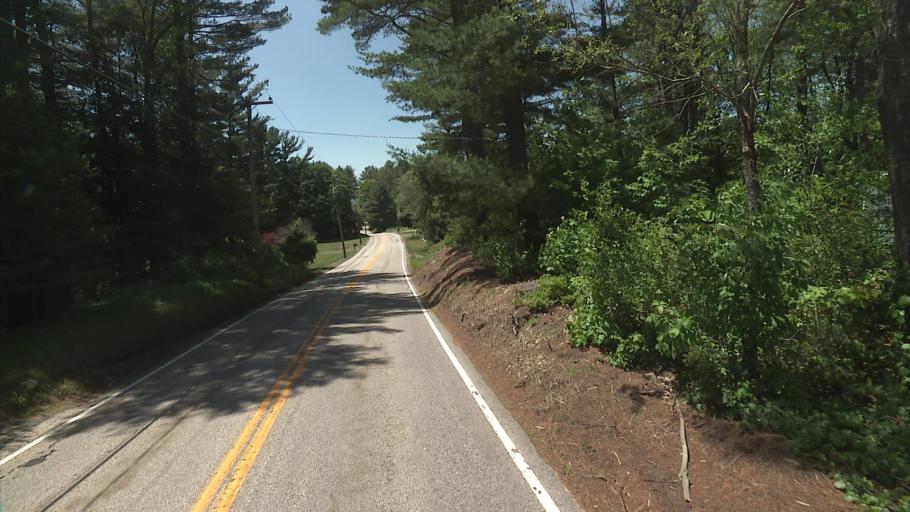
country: US
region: Connecticut
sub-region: Tolland County
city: Stafford Springs
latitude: 41.9745
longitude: -72.3313
